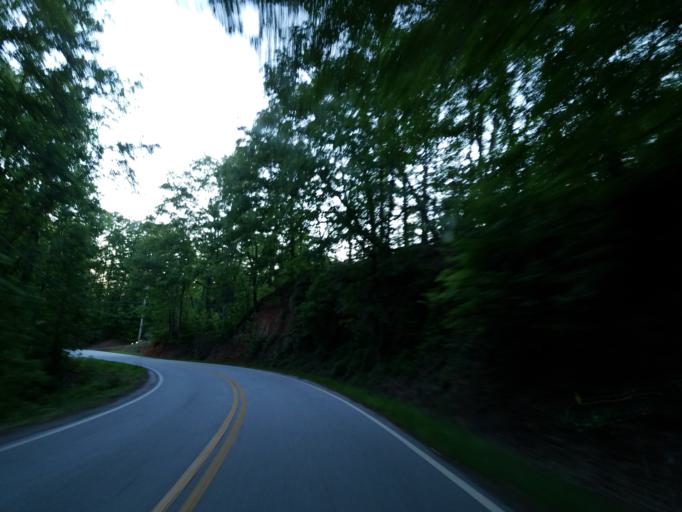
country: US
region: Georgia
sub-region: Lumpkin County
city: Dahlonega
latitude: 34.6111
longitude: -83.9673
